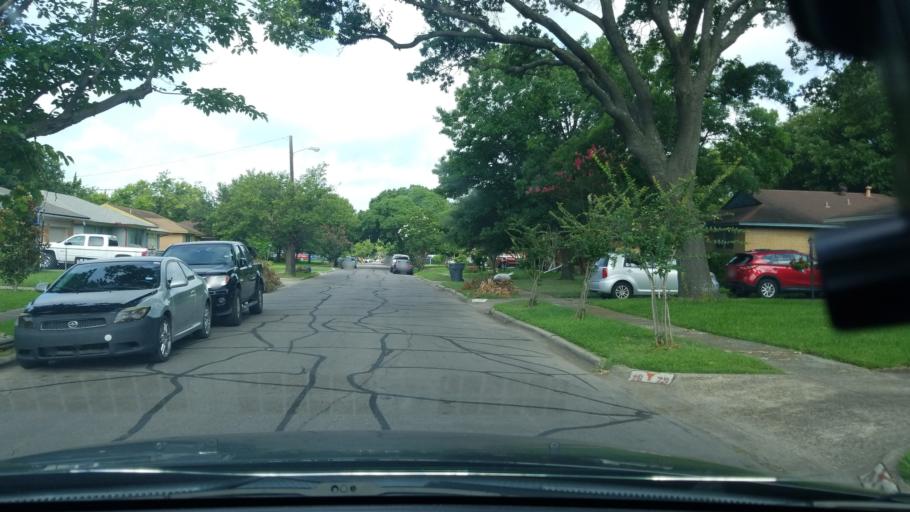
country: US
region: Texas
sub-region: Dallas County
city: Mesquite
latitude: 32.8189
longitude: -96.6697
